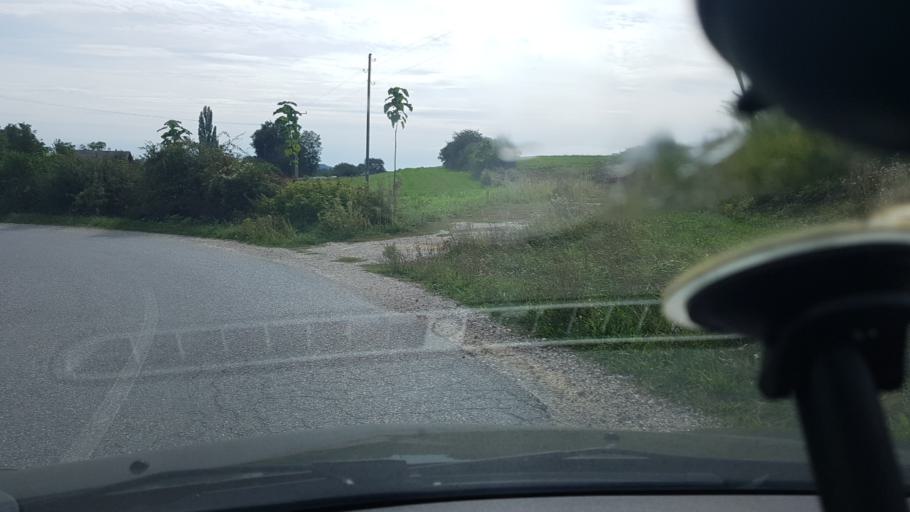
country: HR
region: Varazdinska
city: Ljubescica
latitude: 46.1172
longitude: 16.4212
